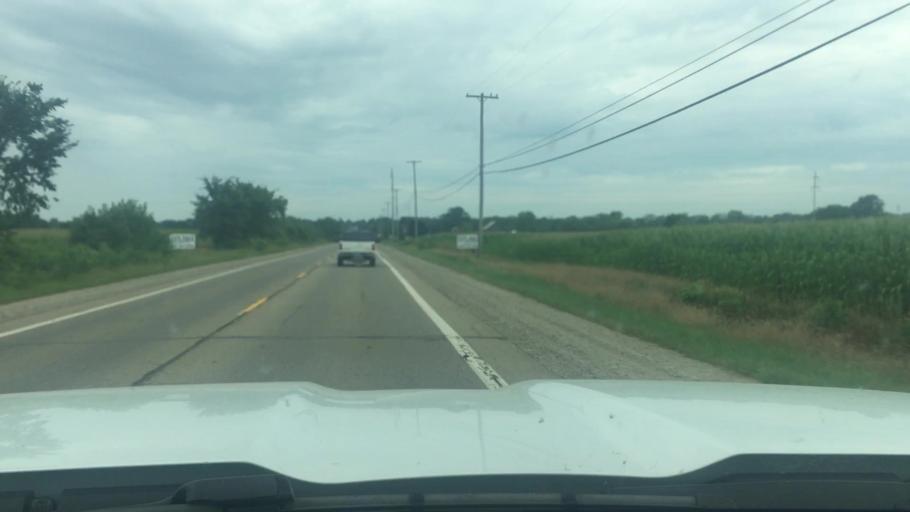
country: US
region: Michigan
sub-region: Clinton County
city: Saint Johns
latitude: 43.0014
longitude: -84.5336
